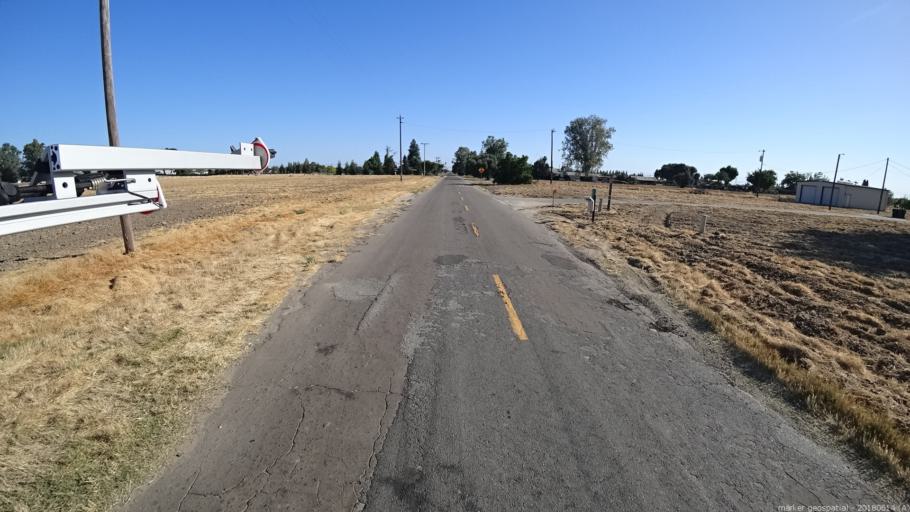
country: US
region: California
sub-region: Madera County
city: Madera
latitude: 36.9505
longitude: -120.1194
